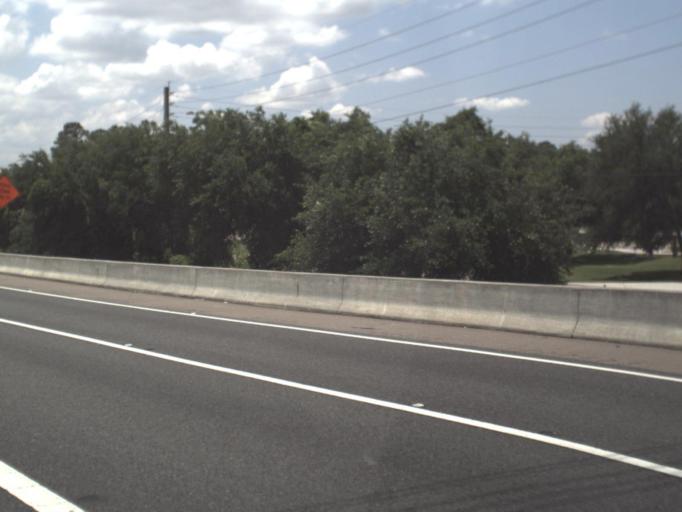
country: US
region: Florida
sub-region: Duval County
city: Jacksonville
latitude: 30.4180
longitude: -81.5659
